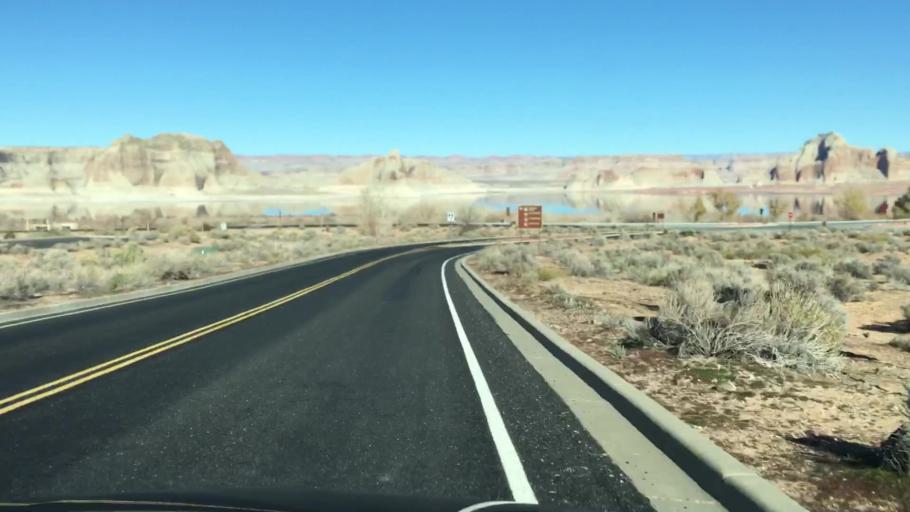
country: US
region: Arizona
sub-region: Coconino County
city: Page
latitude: 36.9944
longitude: -111.4943
